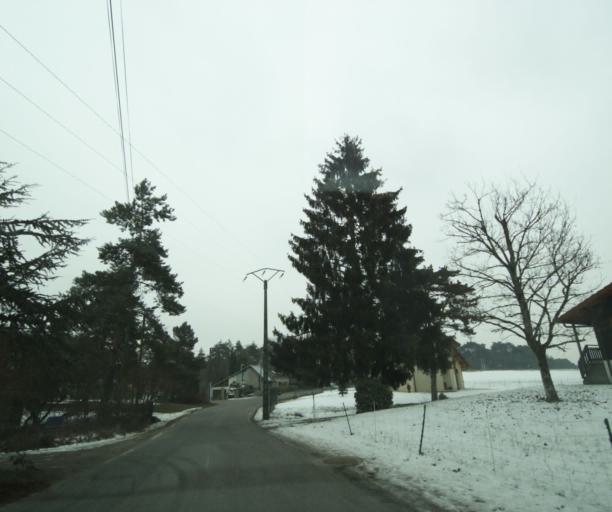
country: FR
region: Rhone-Alpes
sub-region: Departement de la Haute-Savoie
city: Reignier-Esery
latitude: 46.1237
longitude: 6.2839
